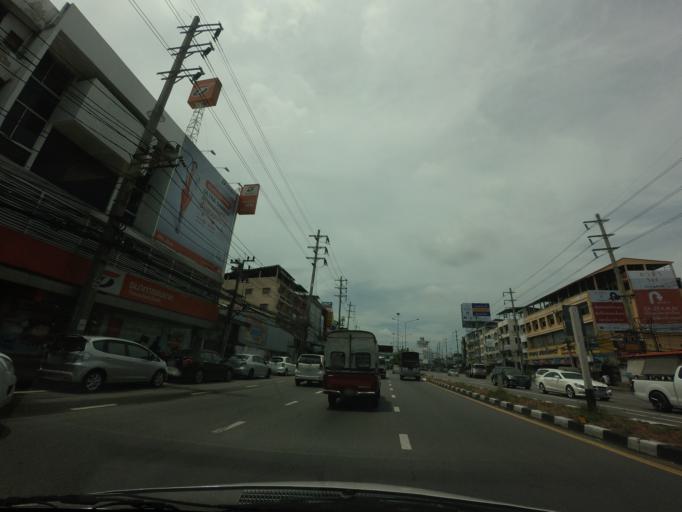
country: TH
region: Bangkok
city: Thung Khru
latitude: 13.6379
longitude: 100.5274
